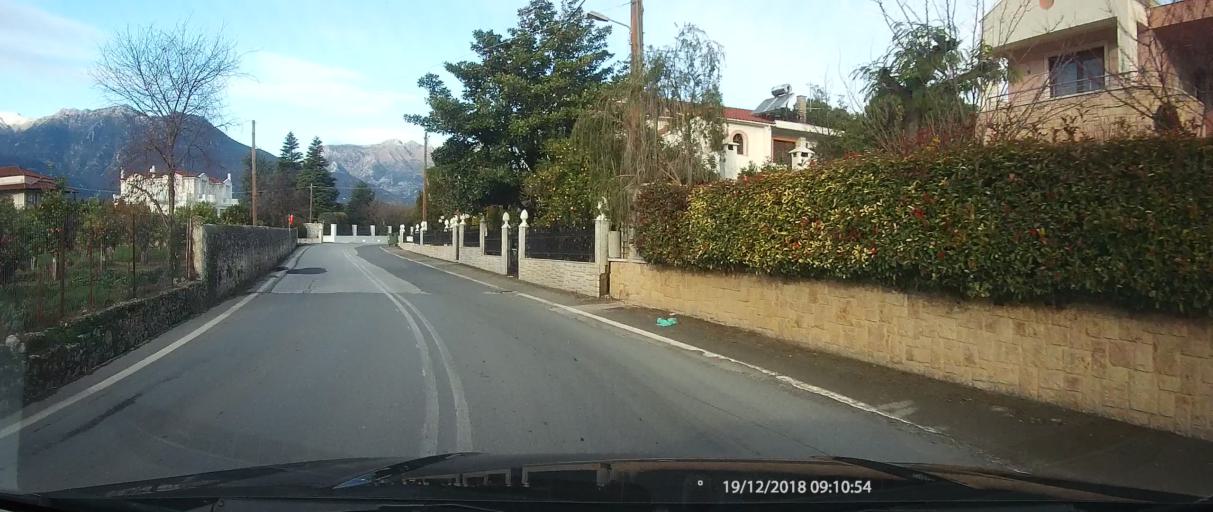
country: GR
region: Peloponnese
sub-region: Nomos Lakonias
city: Sparti
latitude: 37.0773
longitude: 22.4191
